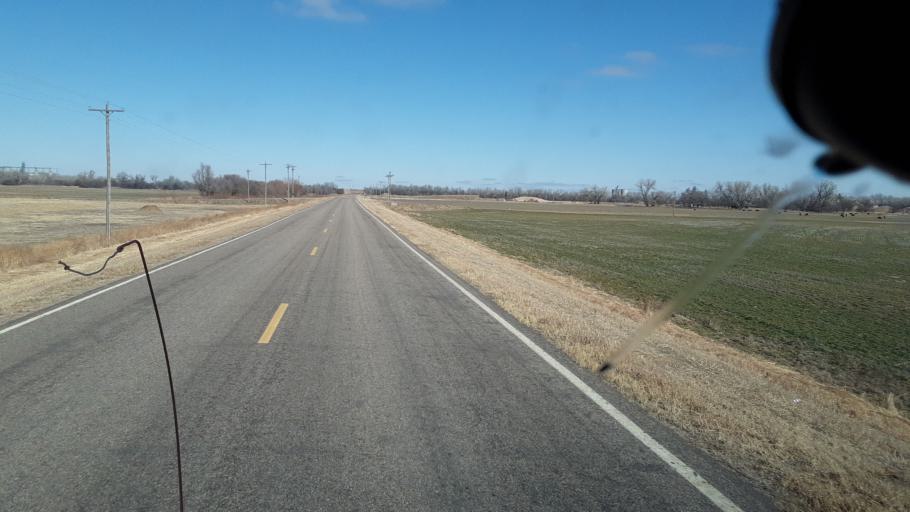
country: US
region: Kansas
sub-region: Barton County
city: Ellinwood
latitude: 38.3454
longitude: -98.6642
